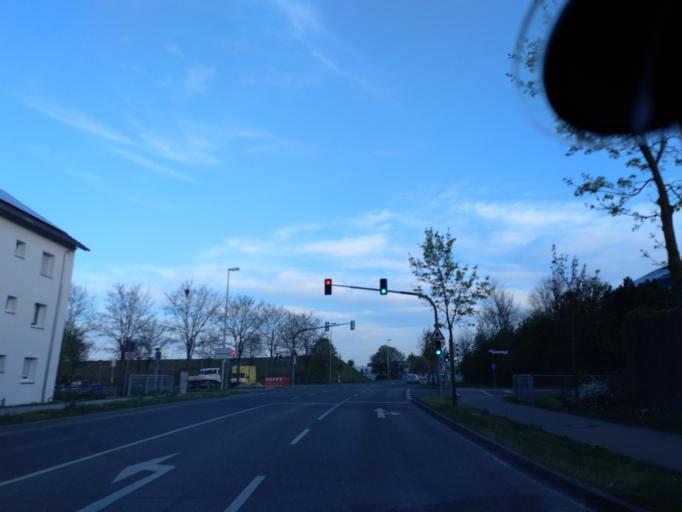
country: DE
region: Baden-Wuerttemberg
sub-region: Regierungsbezirk Stuttgart
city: Crailsheim
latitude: 49.1387
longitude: 10.0351
